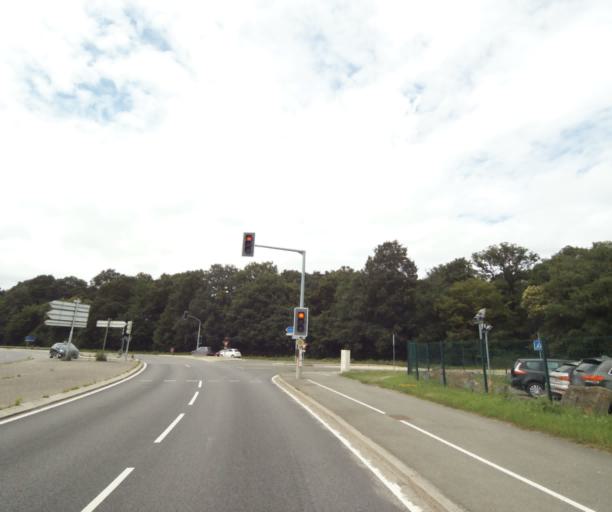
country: FR
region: Ile-de-France
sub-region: Departement des Yvelines
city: Fontenay-le-Fleury
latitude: 48.7979
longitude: 2.0500
